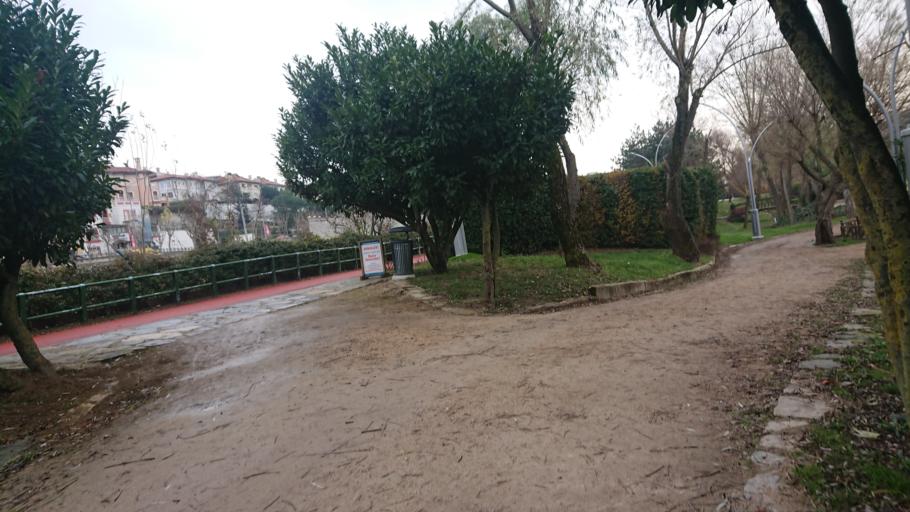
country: TR
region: Istanbul
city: Esenyurt
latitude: 41.0688
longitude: 28.6936
